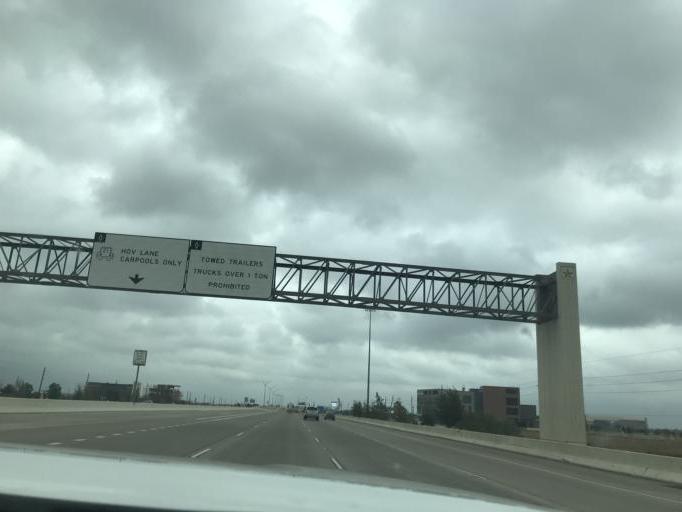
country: US
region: Texas
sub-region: Fort Bend County
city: Greatwood
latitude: 29.5759
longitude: -95.6557
